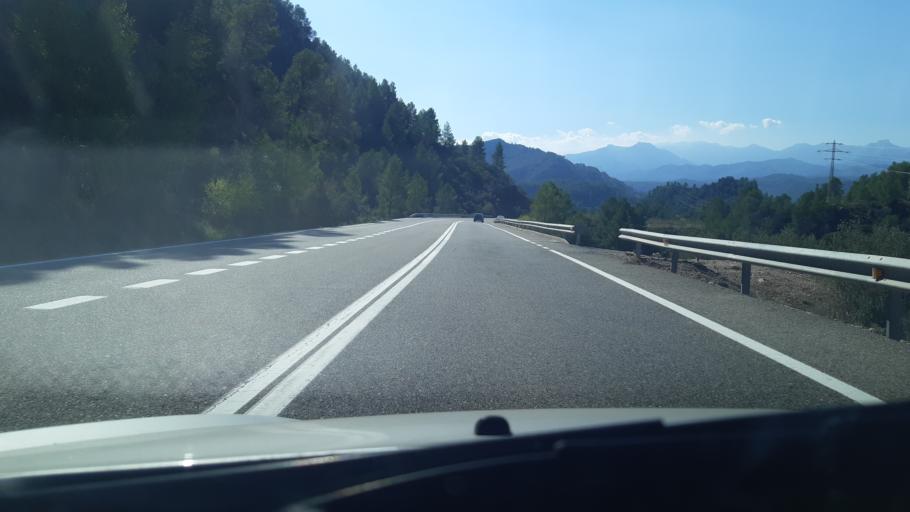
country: ES
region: Catalonia
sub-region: Provincia de Tarragona
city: Benifallet
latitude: 40.9899
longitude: 0.5417
